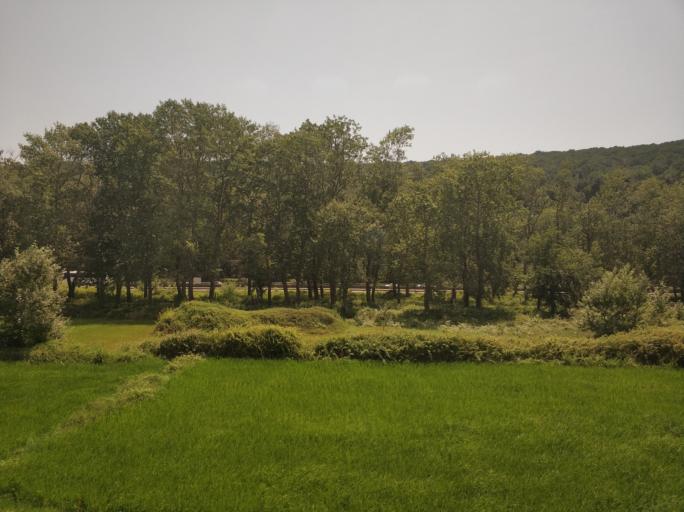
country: IR
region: Gilan
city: Pa'in-e Bazar-e Rudbar
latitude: 36.9581
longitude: 49.5526
